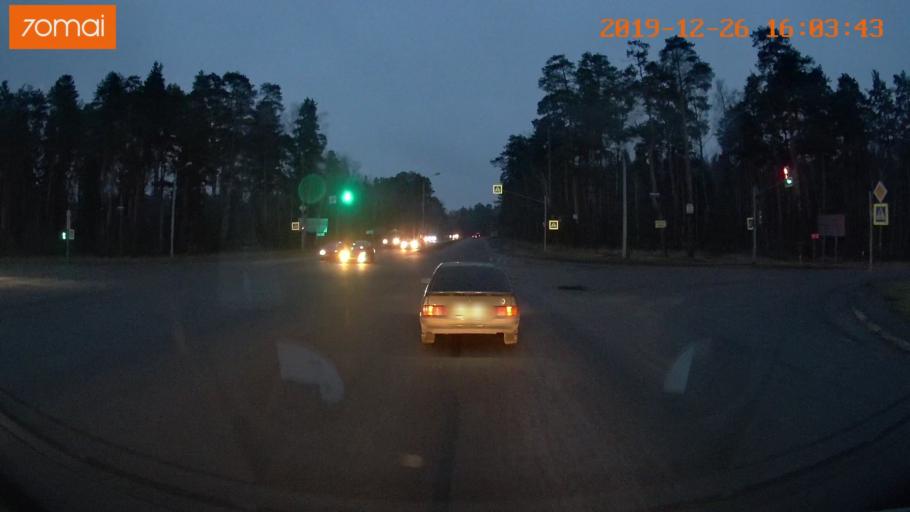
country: RU
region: Jaroslavl
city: Rybinsk
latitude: 58.0104
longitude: 38.8582
